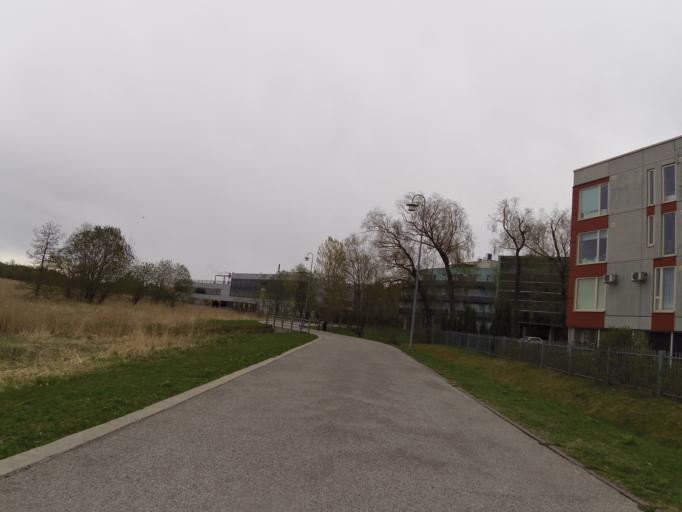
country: EE
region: Harju
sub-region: Saue vald
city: Laagri
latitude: 59.4286
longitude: 24.6616
